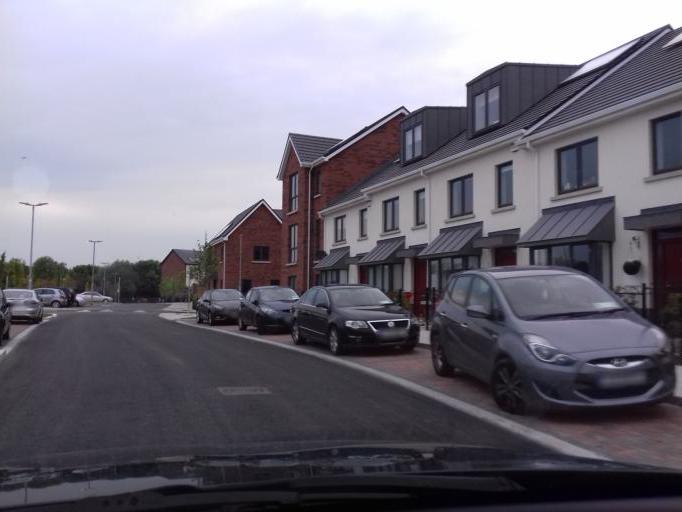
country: IE
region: Leinster
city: Donaghmede
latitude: 53.4054
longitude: -6.1561
